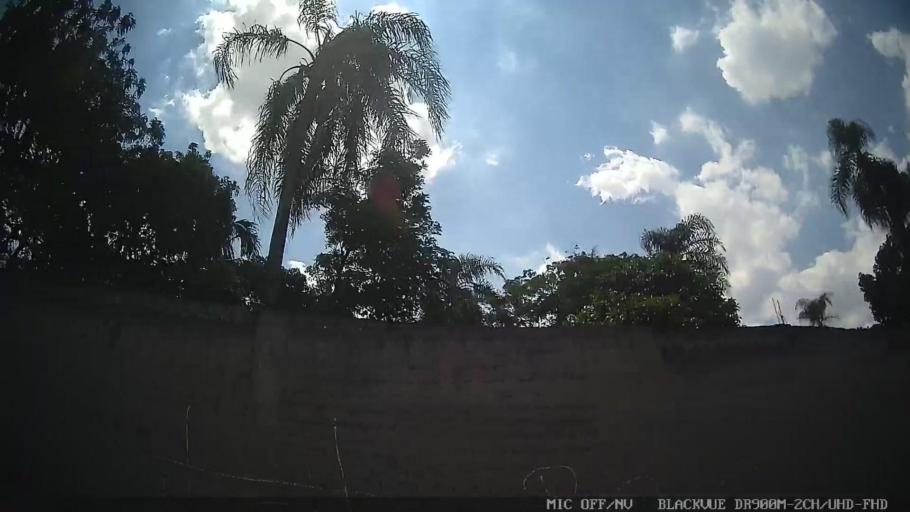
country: BR
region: Sao Paulo
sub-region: Taboao Da Serra
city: Taboao da Serra
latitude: -23.6709
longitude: -46.7865
